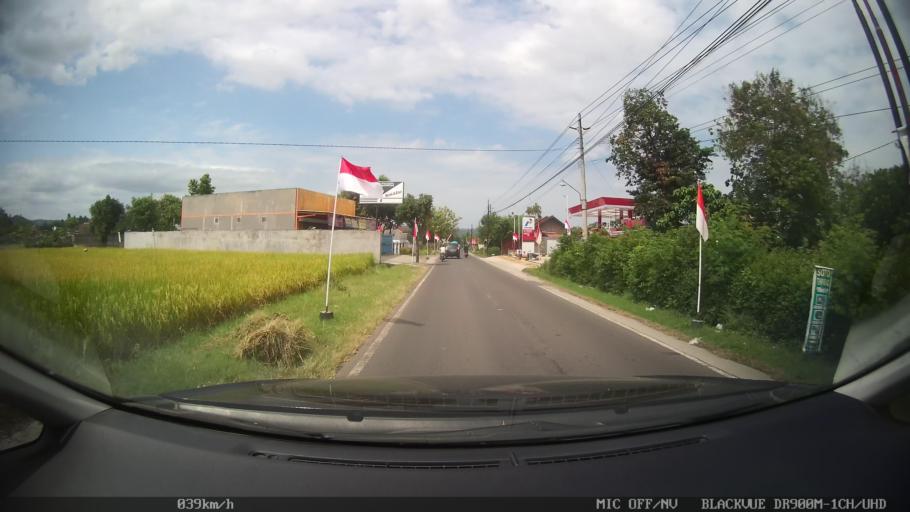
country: ID
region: Daerah Istimewa Yogyakarta
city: Depok
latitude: -7.8139
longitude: 110.4430
